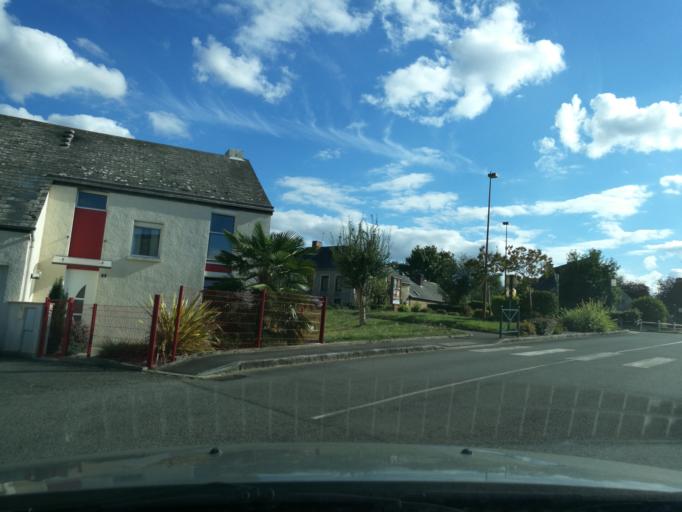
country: FR
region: Brittany
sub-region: Departement d'Ille-et-Vilaine
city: Bedee
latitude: 48.1818
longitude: -1.9494
